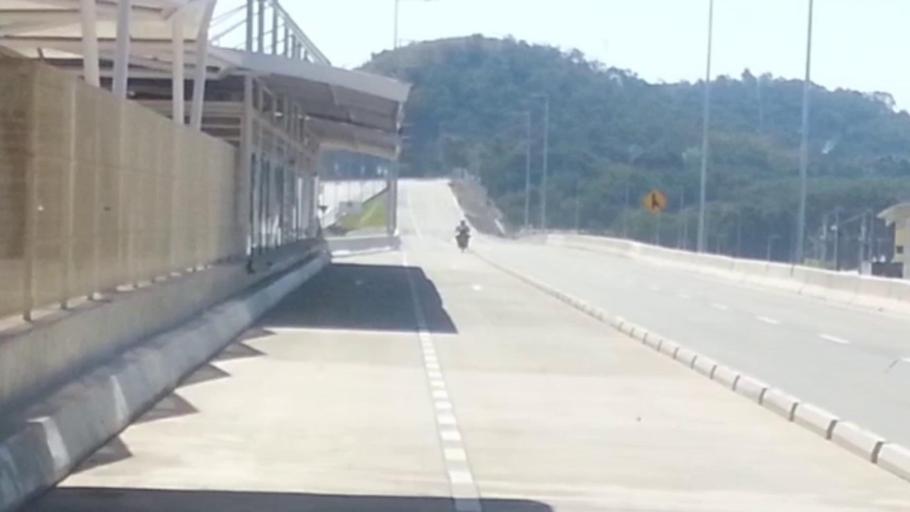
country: BR
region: Rio de Janeiro
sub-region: Nilopolis
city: Nilopolis
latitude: -22.8879
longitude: -43.4009
